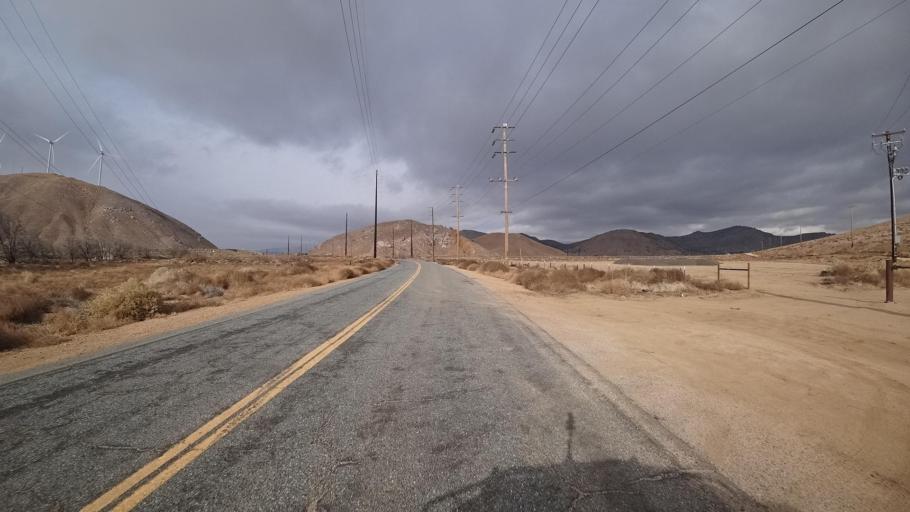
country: US
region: California
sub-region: Kern County
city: Tehachapi
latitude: 35.1097
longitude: -118.3181
